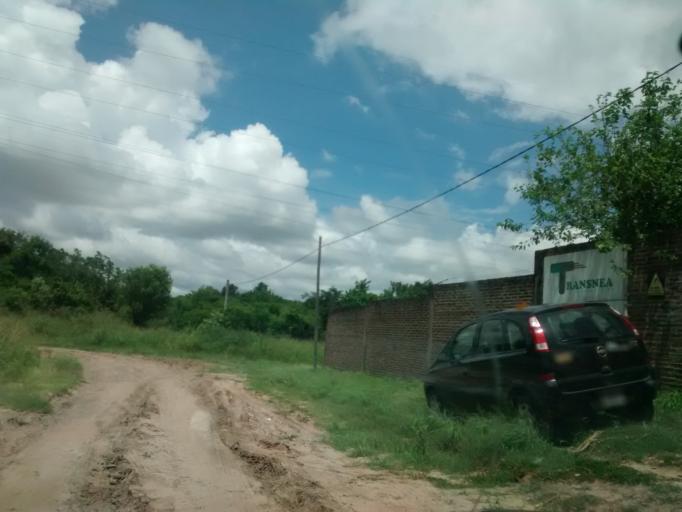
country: AR
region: Chaco
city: Fontana
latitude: -27.4123
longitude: -58.9867
